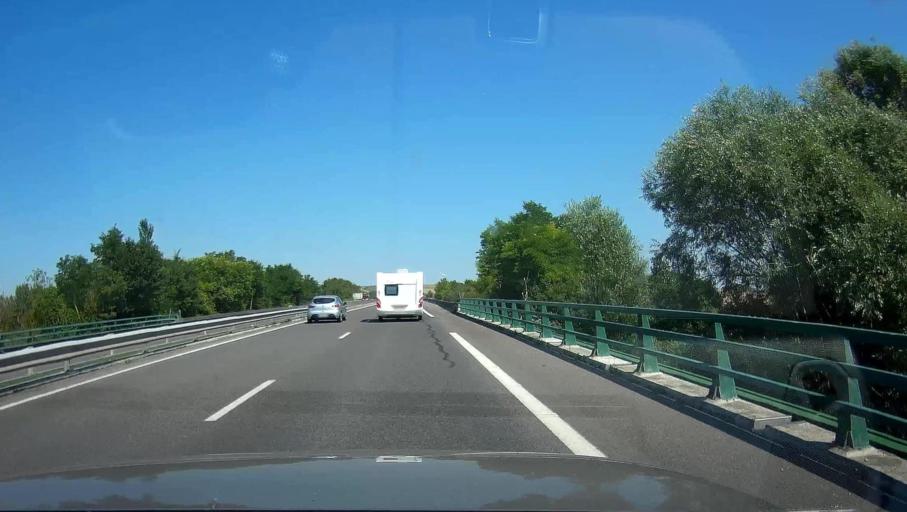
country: FR
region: Champagne-Ardenne
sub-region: Departement de l'Aube
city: Arcis-sur-Aube
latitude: 48.5438
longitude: 4.1886
